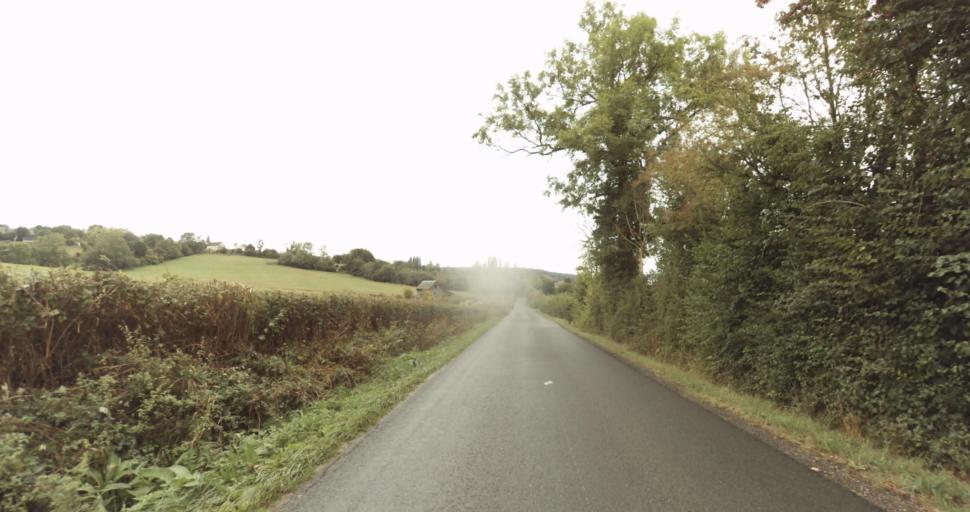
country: FR
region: Lower Normandy
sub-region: Departement de l'Orne
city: Vimoutiers
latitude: 48.8810
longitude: 0.2173
